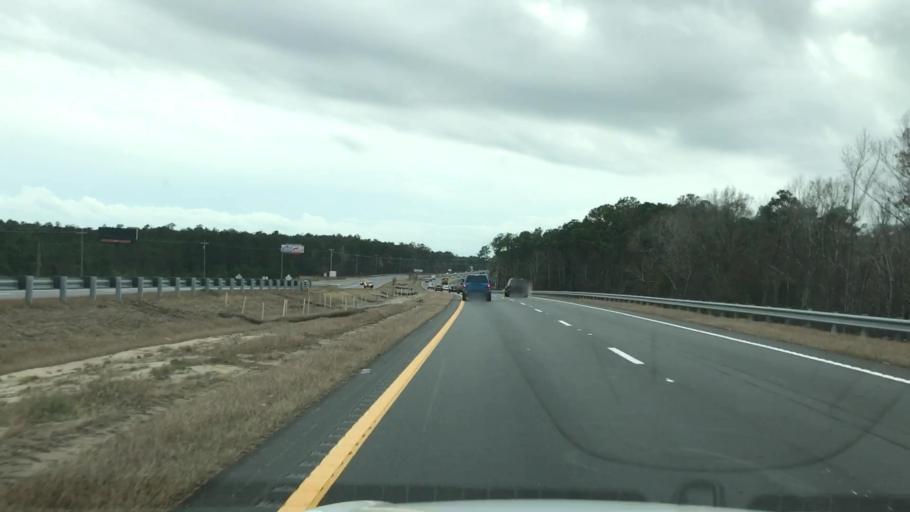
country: US
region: South Carolina
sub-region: Horry County
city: Garden City
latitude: 33.6210
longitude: -79.0049
